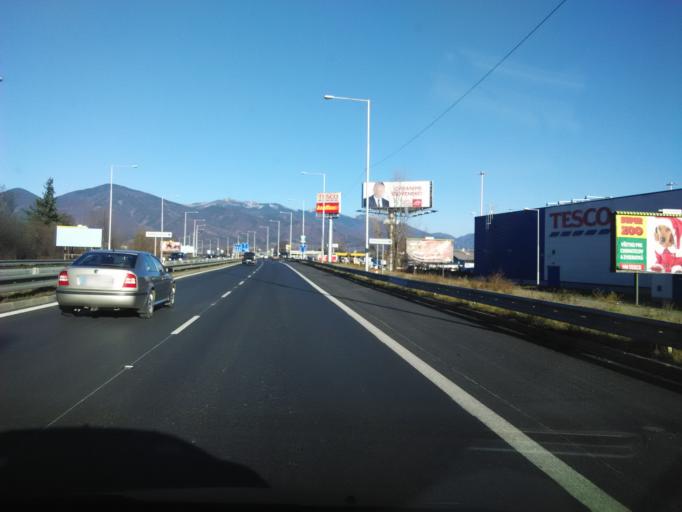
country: SK
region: Zilinsky
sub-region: Okres Martin
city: Martin
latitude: 49.0794
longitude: 18.9195
